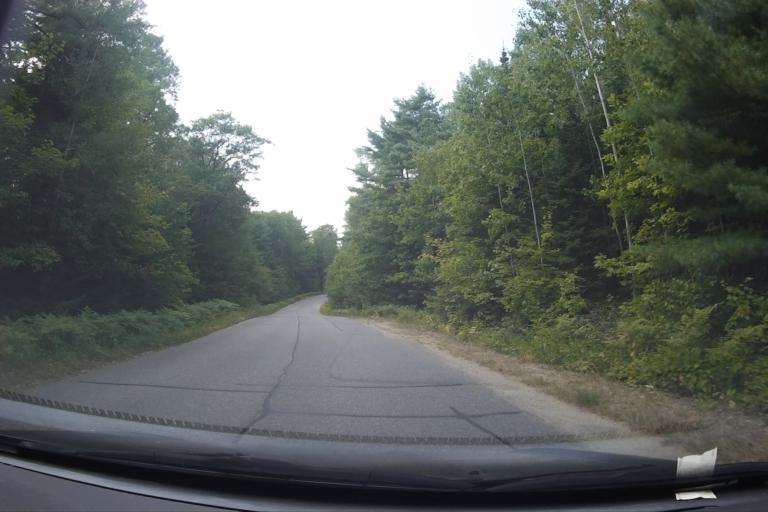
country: CA
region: Ontario
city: Bancroft
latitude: 45.5855
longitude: -78.3608
